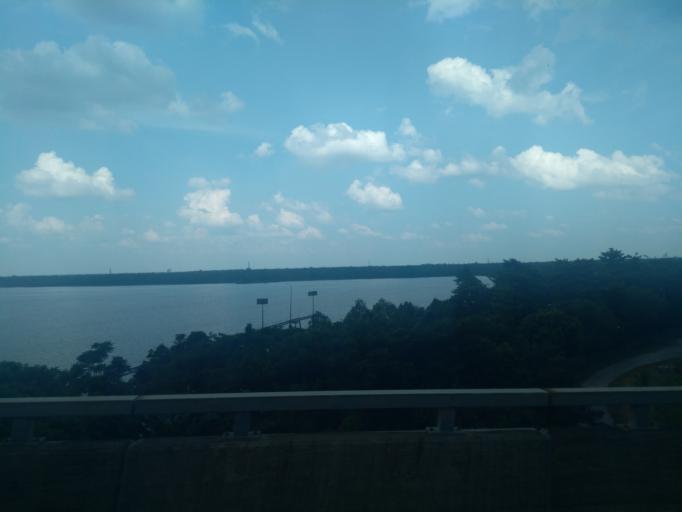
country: MY
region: Sarawak
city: Kuching
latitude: 1.5733
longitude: 110.4093
